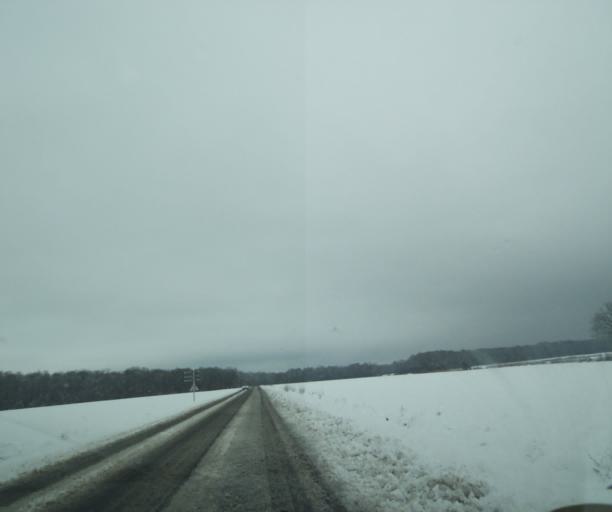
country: FR
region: Champagne-Ardenne
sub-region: Departement de la Haute-Marne
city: Montier-en-Der
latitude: 48.5096
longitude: 4.7478
